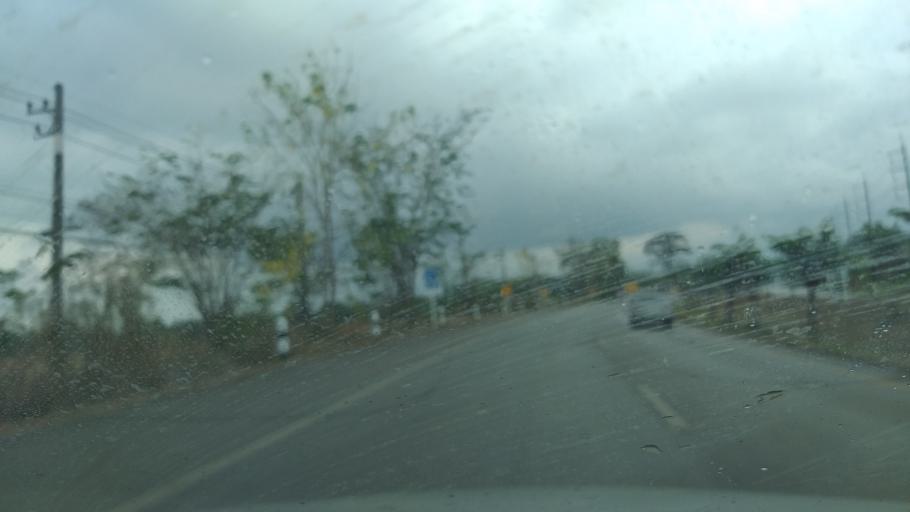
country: TH
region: Chanthaburi
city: Khlung
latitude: 12.4477
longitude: 102.2885
